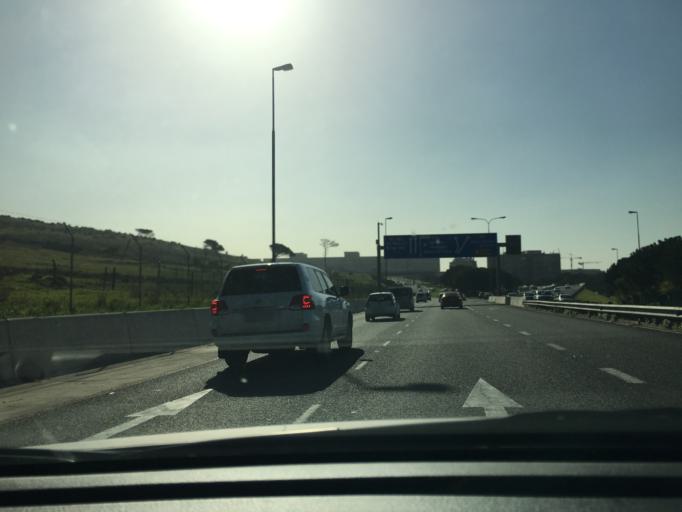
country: ZA
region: Western Cape
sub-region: City of Cape Town
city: Rosebank
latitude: -33.9489
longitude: 18.4668
